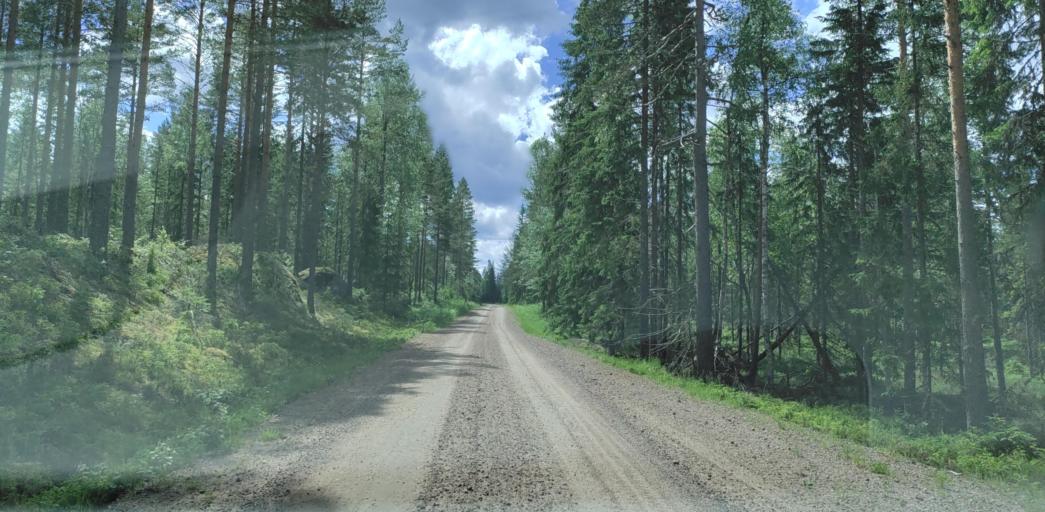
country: SE
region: Vaermland
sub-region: Hagfors Kommun
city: Ekshaerad
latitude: 60.0986
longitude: 13.3492
